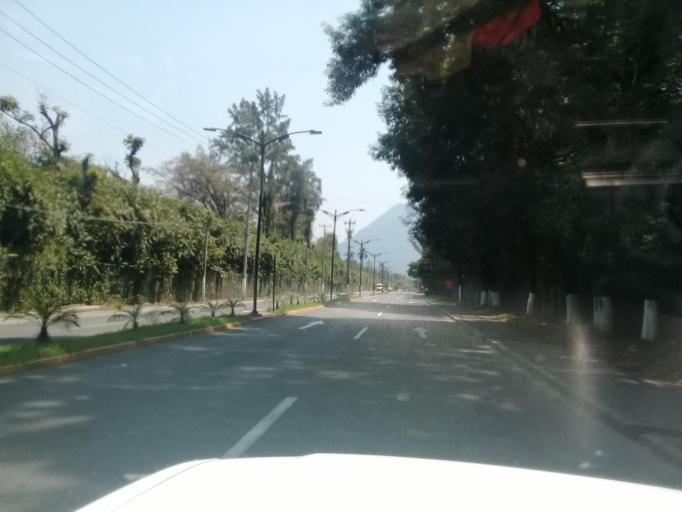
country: MX
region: Veracruz
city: Ixtac Zoquitlan
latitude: 18.8618
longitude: -97.0453
